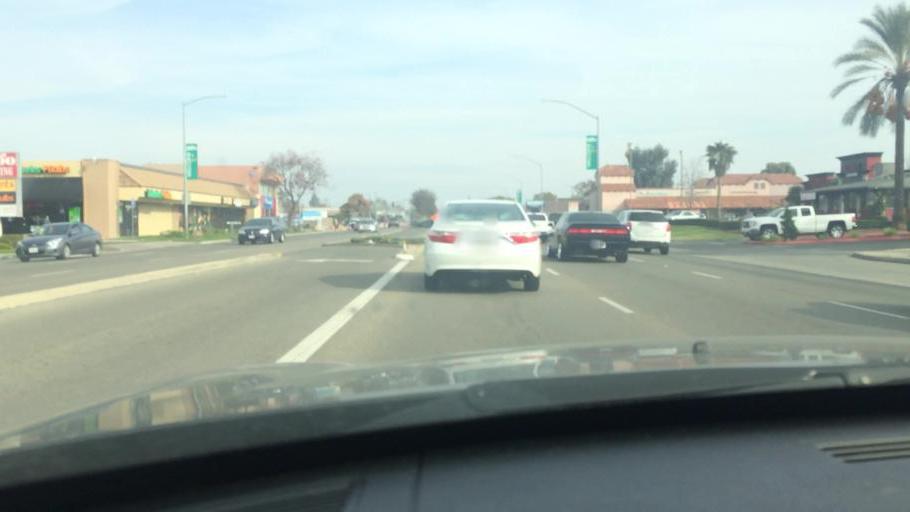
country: US
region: California
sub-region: Fresno County
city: Tarpey Village
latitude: 36.8084
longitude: -119.7118
